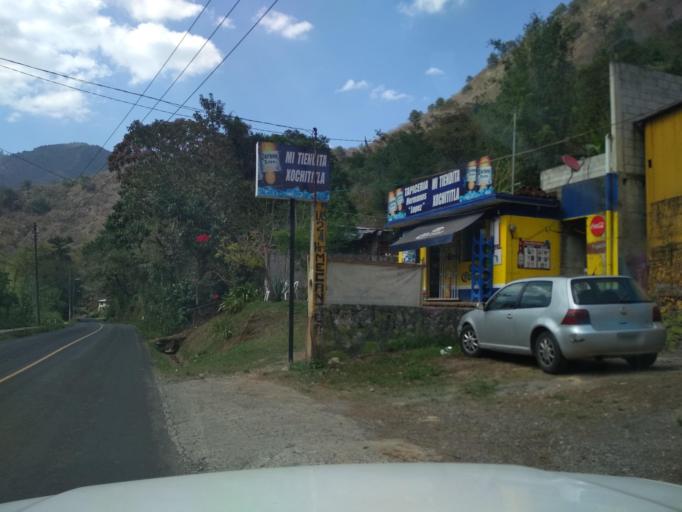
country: MX
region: Veracruz
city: Jalapilla
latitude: 18.7914
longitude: -97.0965
